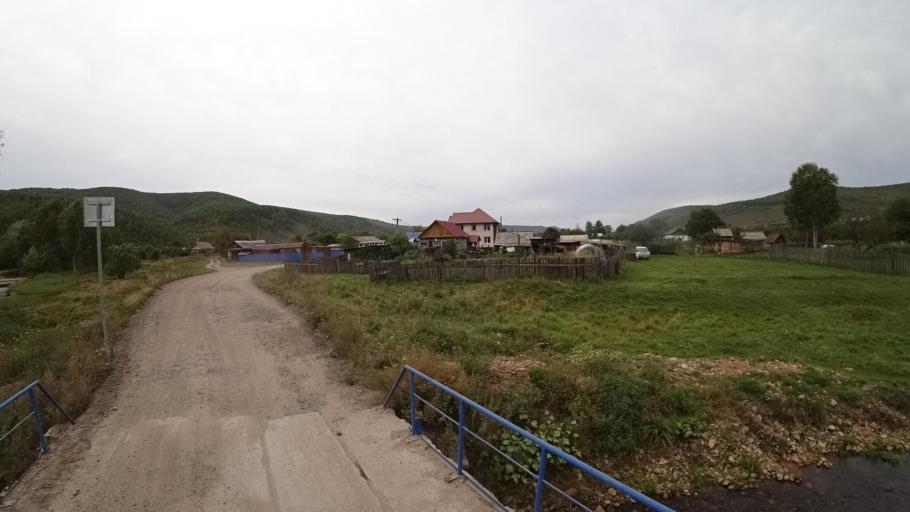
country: RU
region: Jewish Autonomous Oblast
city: Khingansk
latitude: 49.0311
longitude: 131.0494
